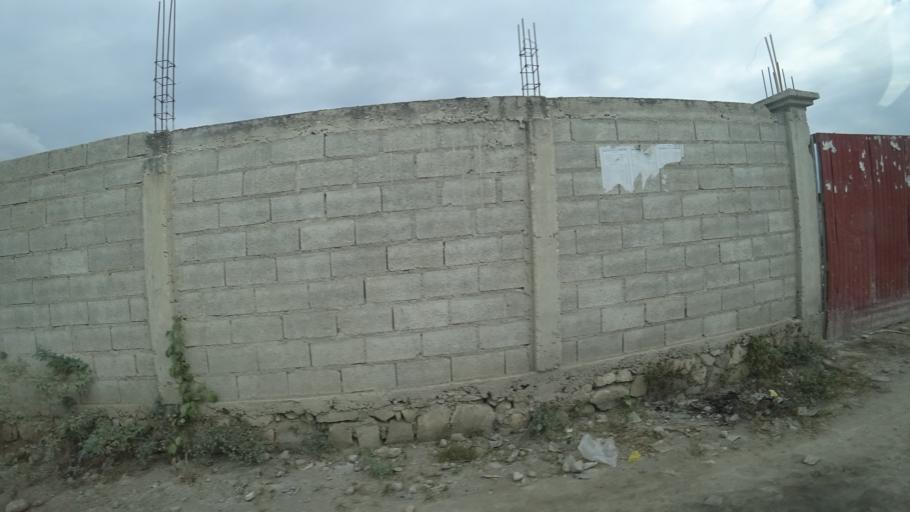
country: HT
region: Ouest
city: Croix des Bouquets
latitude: 18.6498
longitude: -72.2569
